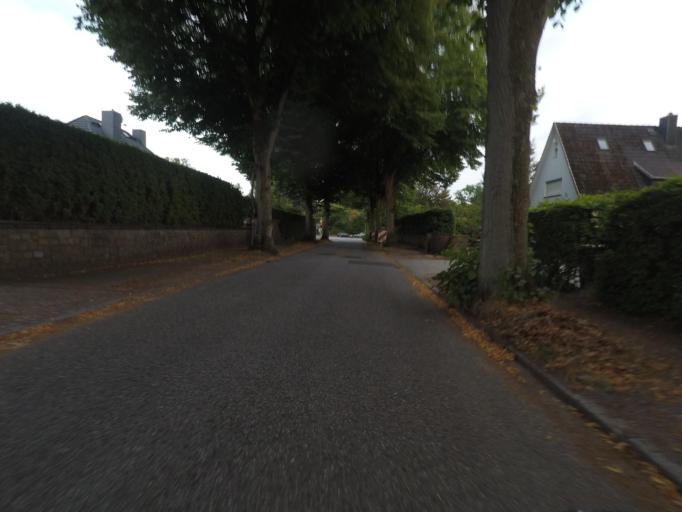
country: DE
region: Hamburg
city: Wellingsbuettel
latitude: 53.6466
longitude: 10.0724
